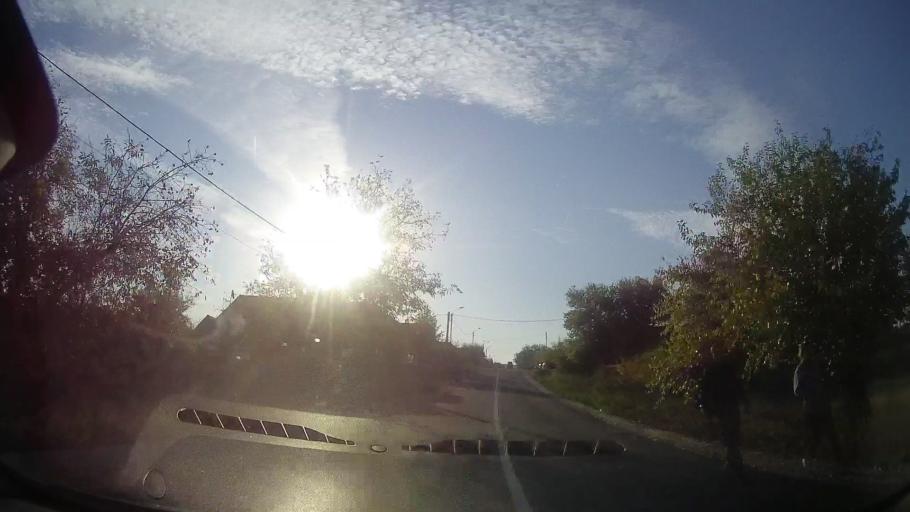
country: RO
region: Timis
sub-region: Comuna Masloc
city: Masloc
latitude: 45.9692
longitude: 21.4767
